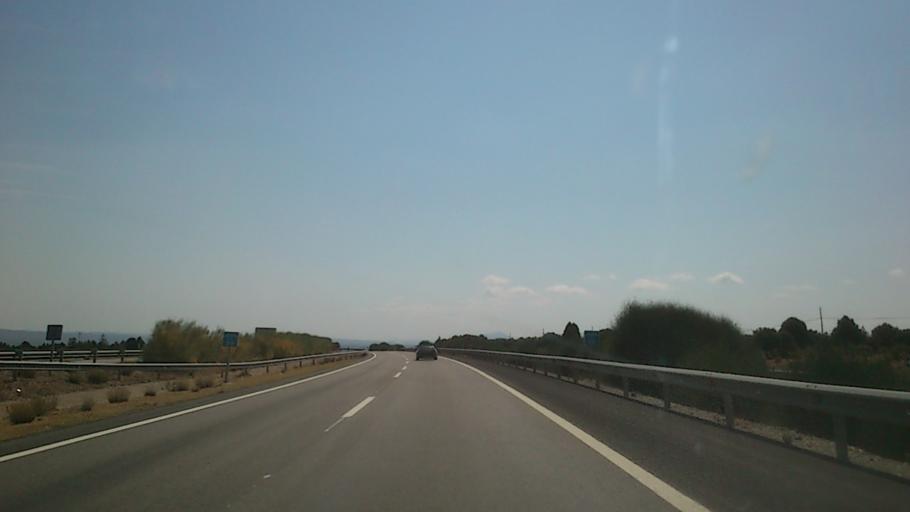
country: ES
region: Aragon
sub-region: Provincia de Teruel
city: Valbona
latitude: 40.1897
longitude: -0.9051
